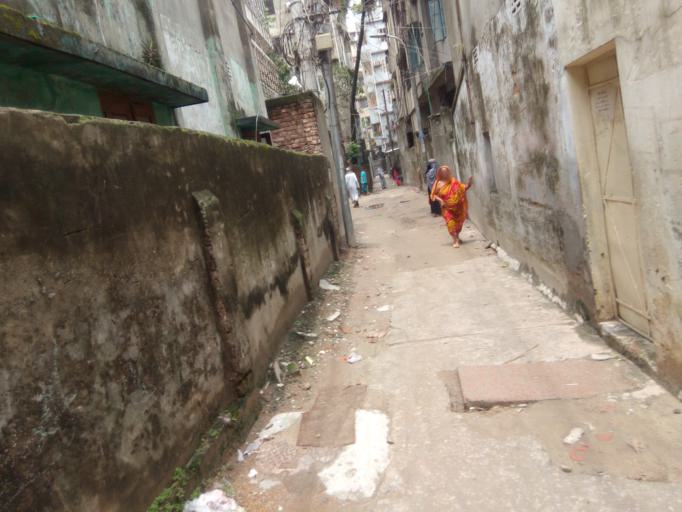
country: BD
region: Dhaka
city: Azimpur
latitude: 23.7430
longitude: 90.3674
